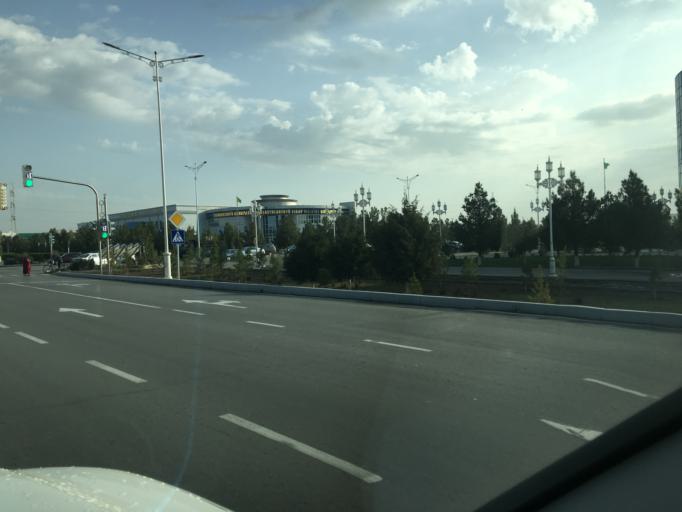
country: TM
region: Lebap
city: Turkmenabat
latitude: 39.0719
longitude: 63.5870
